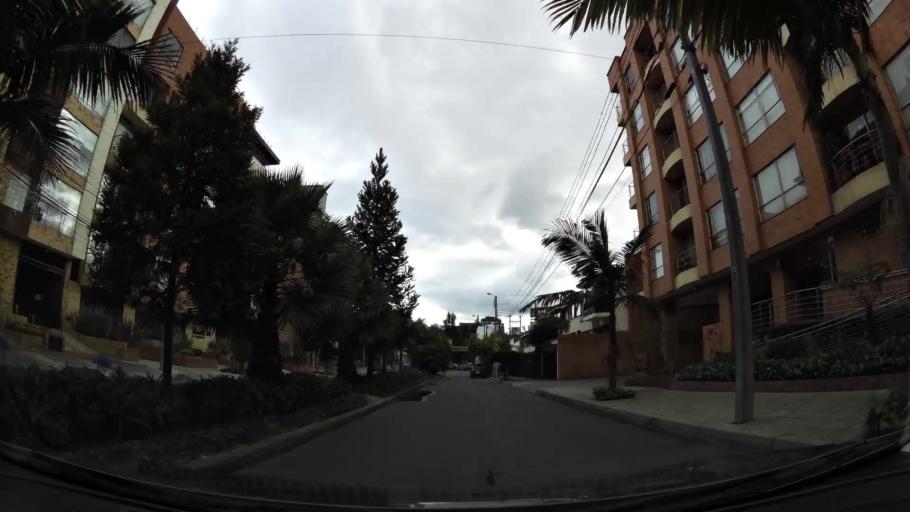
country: CO
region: Bogota D.C.
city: Barrio San Luis
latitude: 4.6882
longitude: -74.0442
